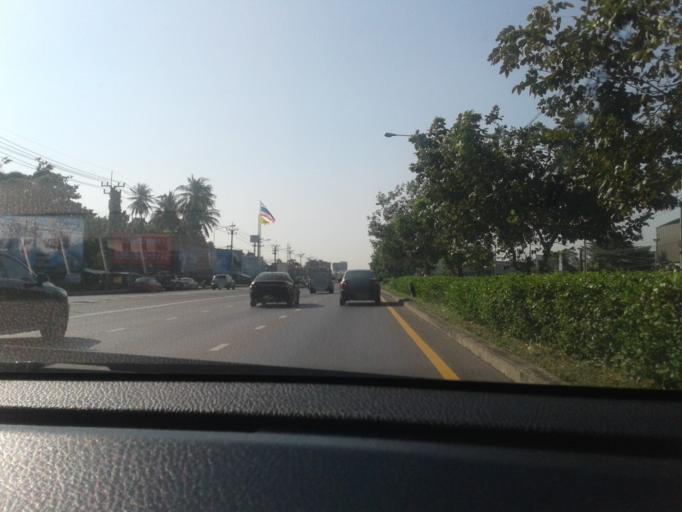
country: TH
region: Bangkok
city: Taling Chan
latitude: 13.7654
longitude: 100.4447
